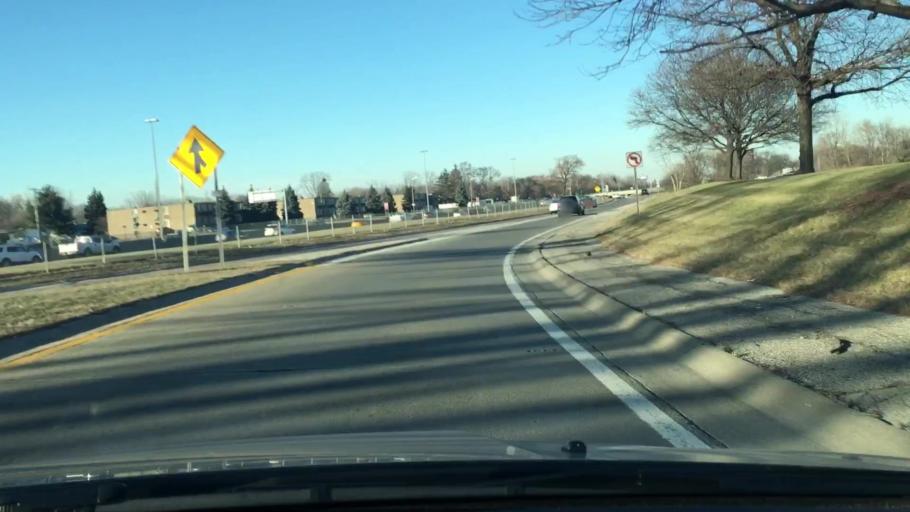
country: US
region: Michigan
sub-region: Wayne County
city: Dearborn
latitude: 42.3316
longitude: -83.2151
